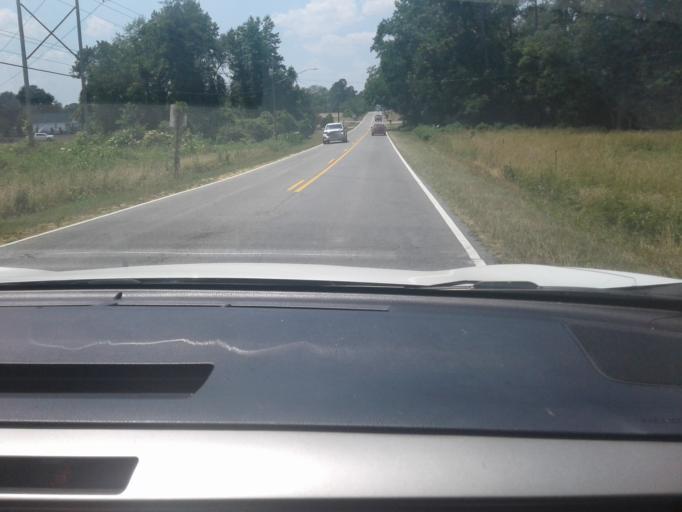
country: US
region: North Carolina
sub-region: Johnston County
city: Benson
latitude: 35.3874
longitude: -78.5615
